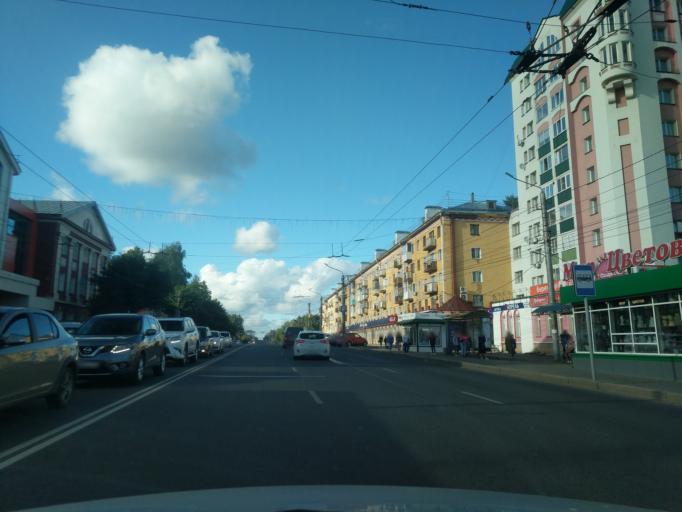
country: RU
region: Kirov
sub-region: Kirovo-Chepetskiy Rayon
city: Kirov
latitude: 58.5944
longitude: 49.6818
